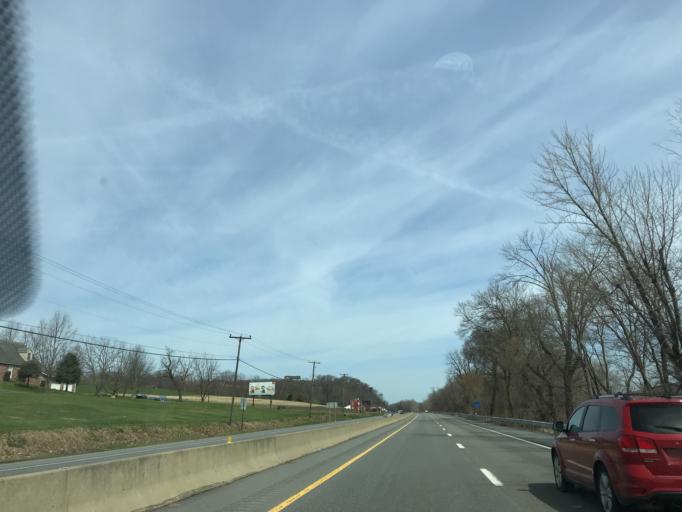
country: US
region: Pennsylvania
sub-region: Snyder County
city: Selinsgrove
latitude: 40.7330
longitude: -76.8557
